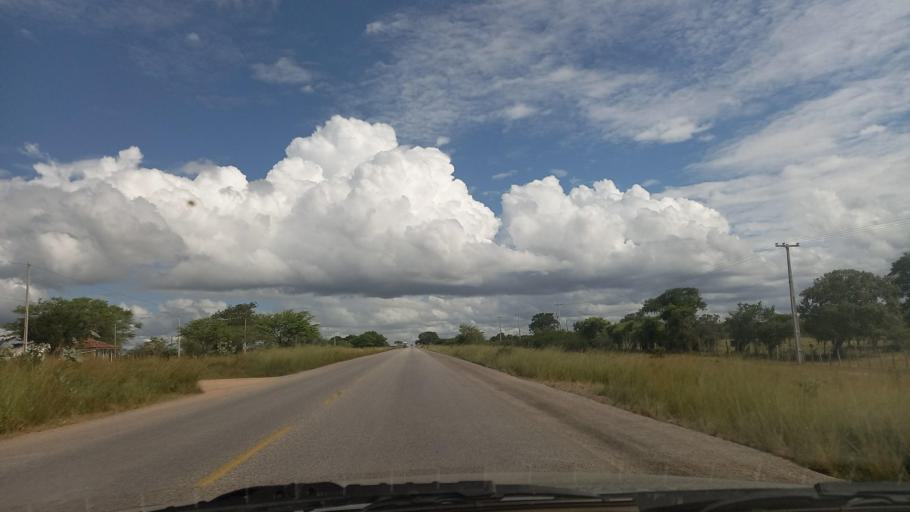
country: BR
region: Pernambuco
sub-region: Cachoeirinha
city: Cachoeirinha
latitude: -8.4595
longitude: -36.2150
